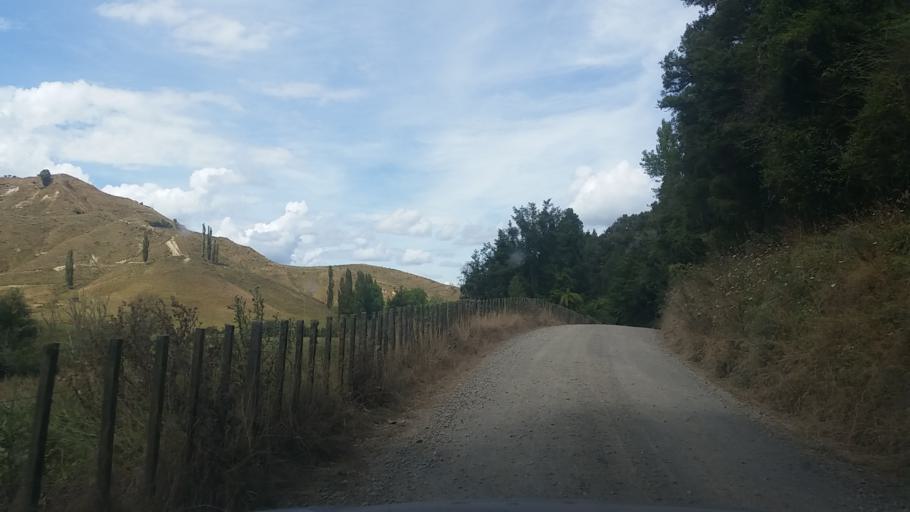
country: NZ
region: Taranaki
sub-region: New Plymouth District
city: Waitara
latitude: -39.0918
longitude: 174.8388
